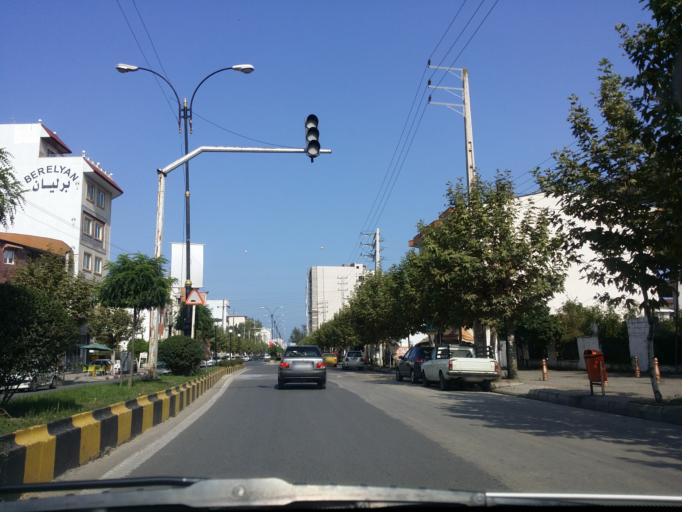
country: IR
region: Mazandaran
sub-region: Nowshahr
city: Nowshahr
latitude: 36.6434
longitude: 51.4915
